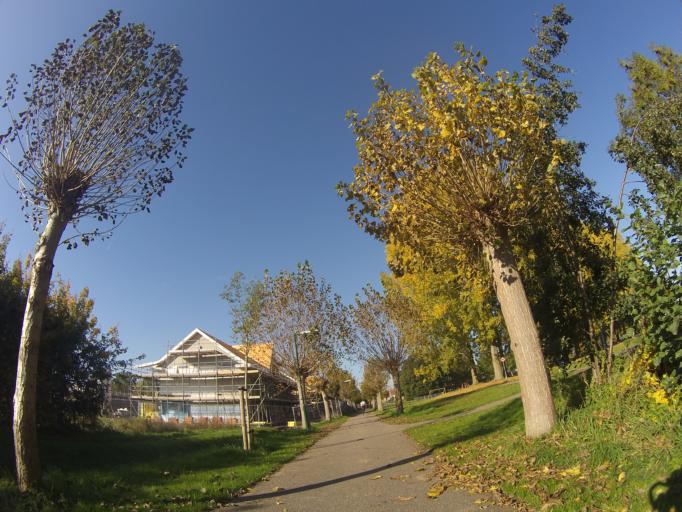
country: NL
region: Utrecht
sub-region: Gemeente Houten
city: Houten
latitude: 52.0270
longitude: 5.1531
